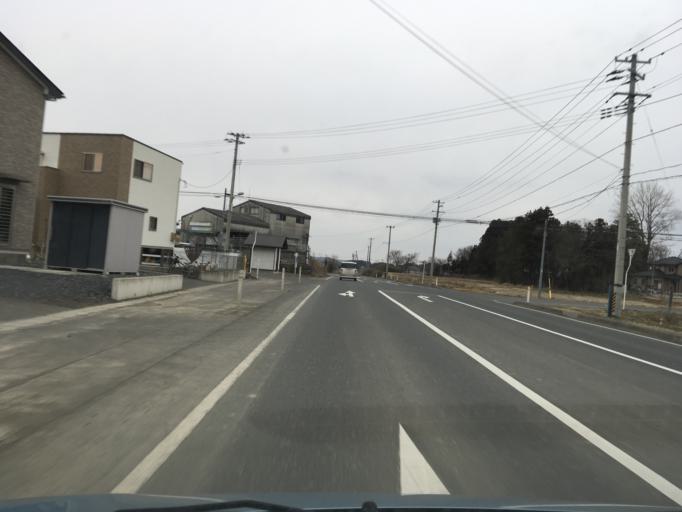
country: JP
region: Miyagi
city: Wakuya
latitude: 38.6741
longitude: 141.2700
